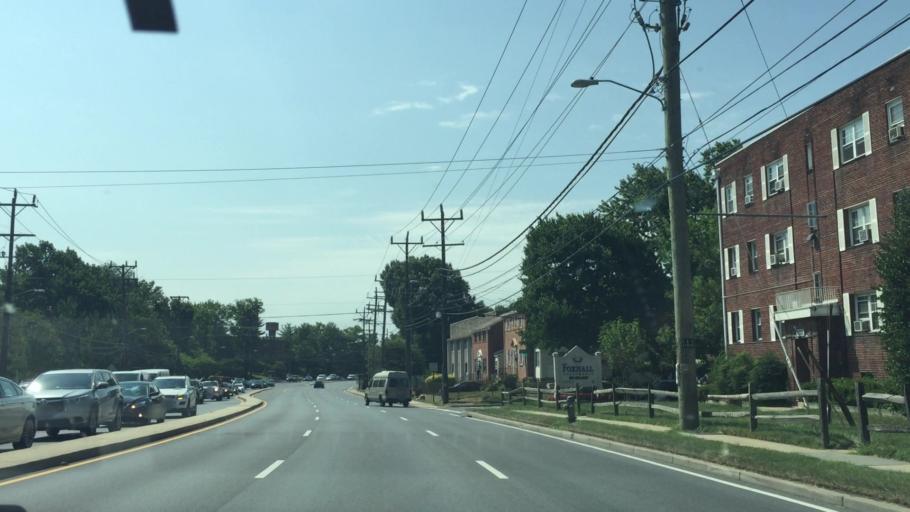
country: US
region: Maryland
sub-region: Prince George's County
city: Langley Park
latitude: 38.9987
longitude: -76.9950
